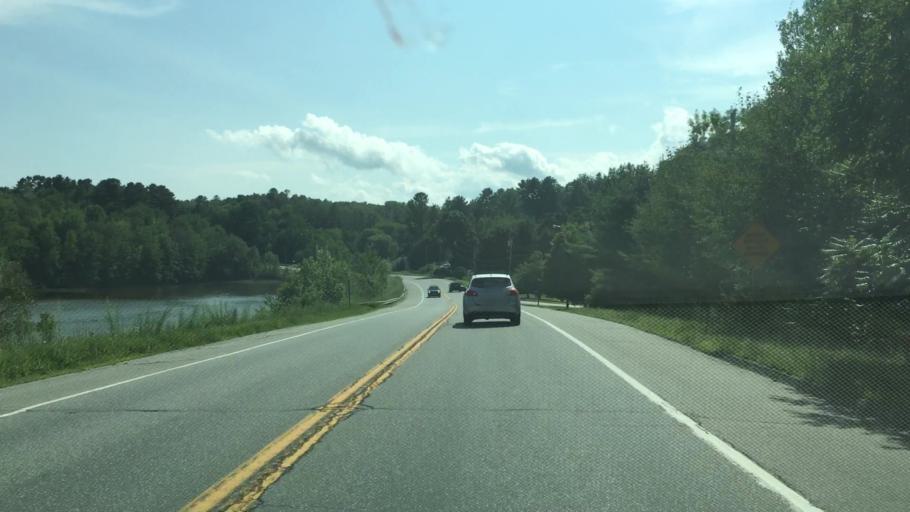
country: US
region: Maine
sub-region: Penobscot County
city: Orrington
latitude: 44.6976
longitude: -68.8457
